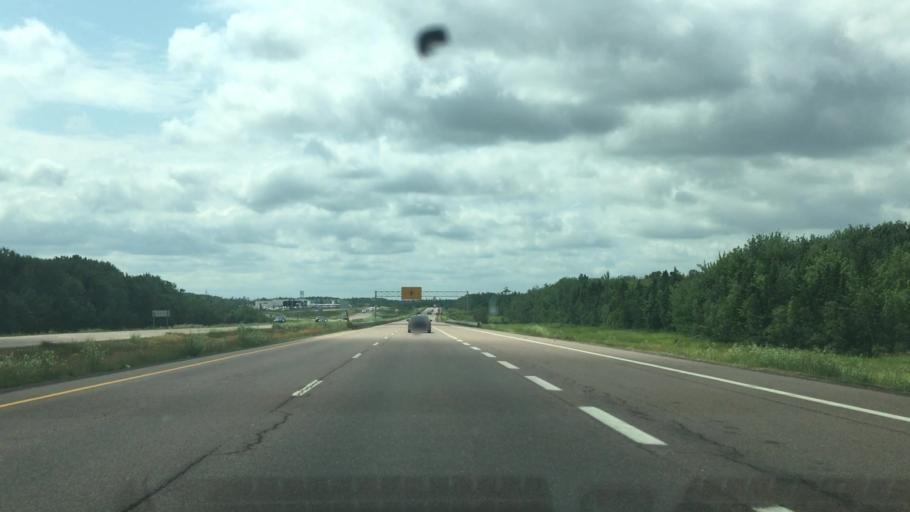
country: CA
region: New Brunswick
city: Dieppe
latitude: 46.1227
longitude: -64.6885
